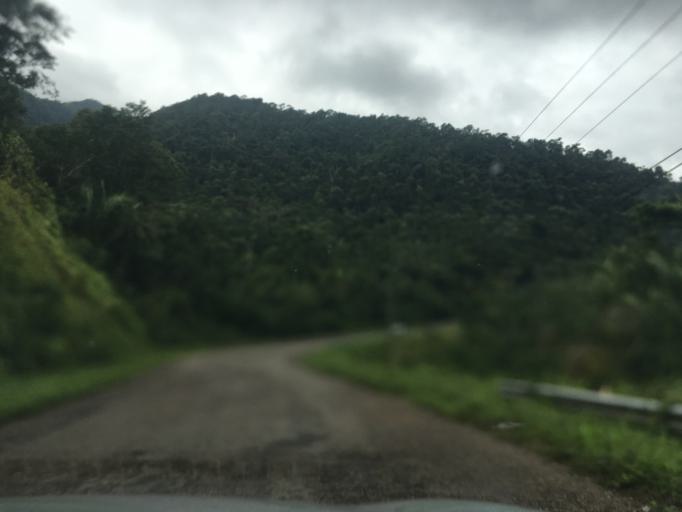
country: BZ
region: Cayo
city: Belmopan
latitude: 17.0561
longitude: -88.5834
